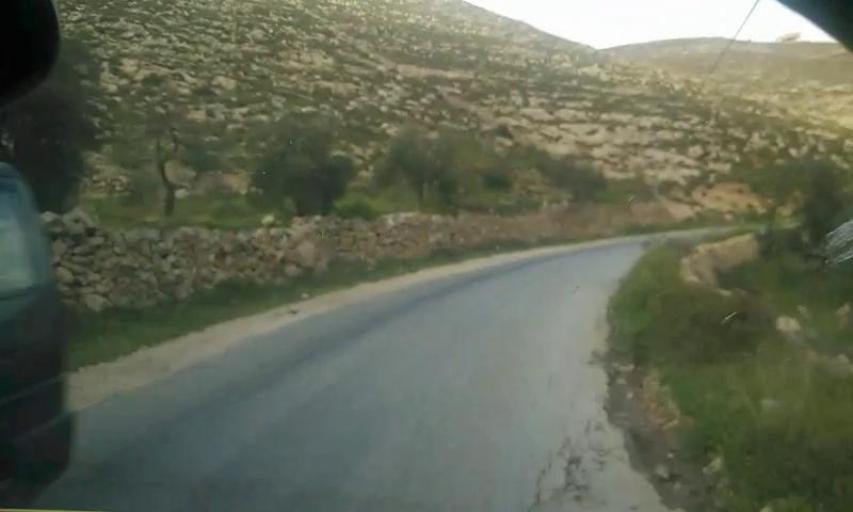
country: PS
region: West Bank
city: Ash Shuyukh
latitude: 31.5927
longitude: 35.1616
